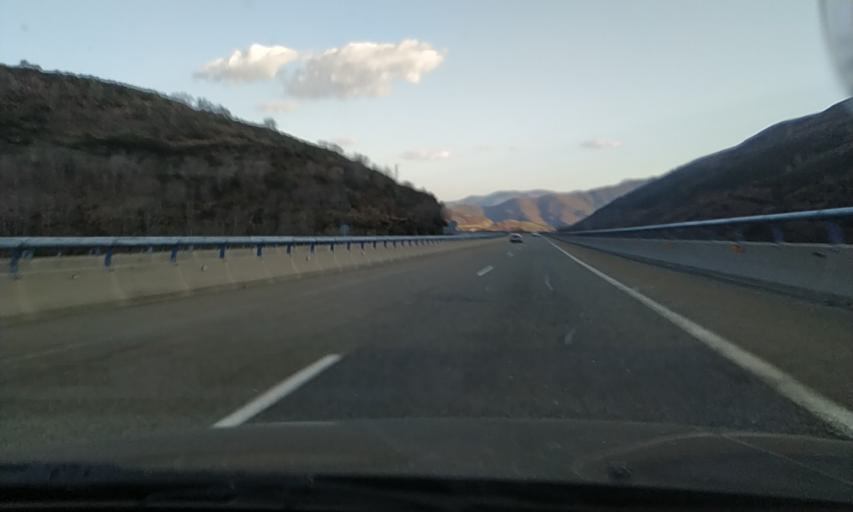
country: ES
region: Castille and Leon
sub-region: Provincia de Leon
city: Vega de Valcarce
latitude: 42.7101
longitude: -7.0091
